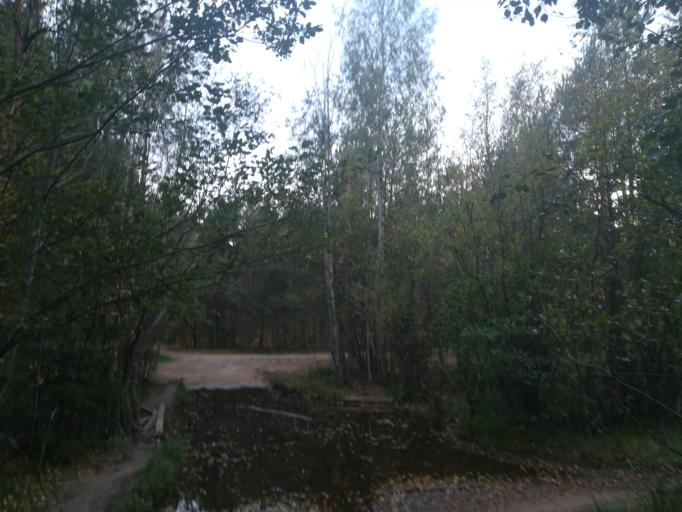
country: RU
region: Leningrad
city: Priozersk
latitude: 61.0406
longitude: 30.1905
